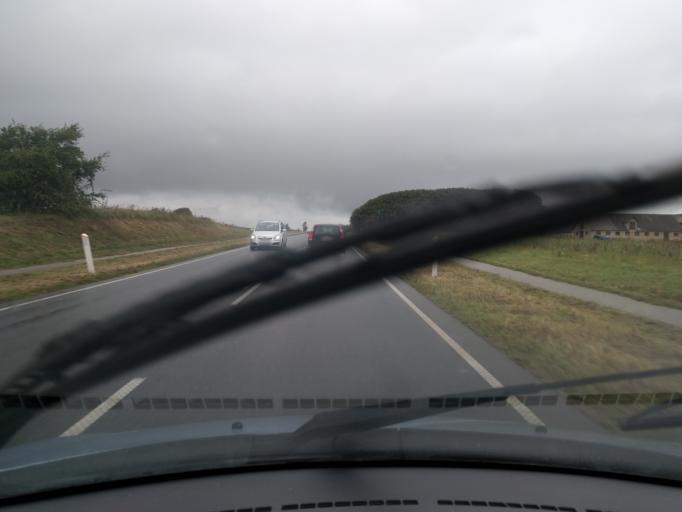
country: DK
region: Zealand
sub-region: Naestved Kommune
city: Naestved
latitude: 55.1418
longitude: 11.8186
